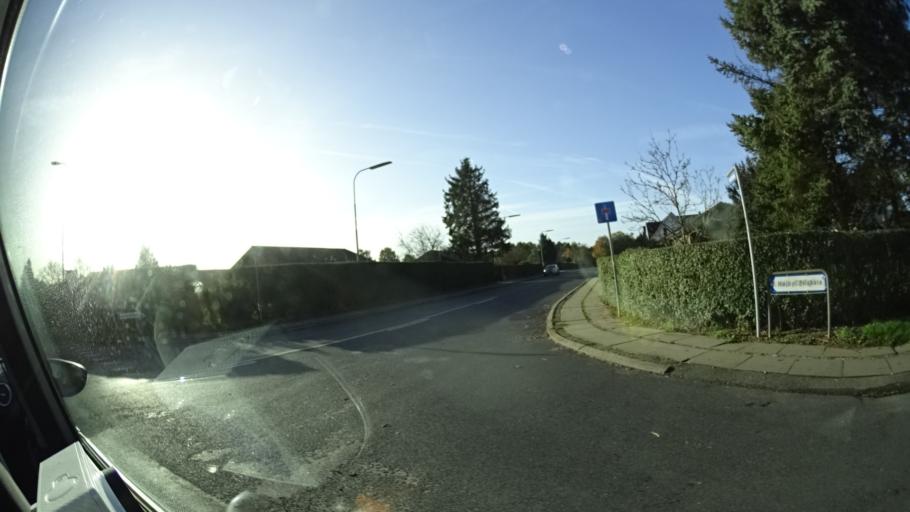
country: DK
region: South Denmark
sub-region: Odense Kommune
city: Hojby
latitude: 55.3400
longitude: 10.4330
